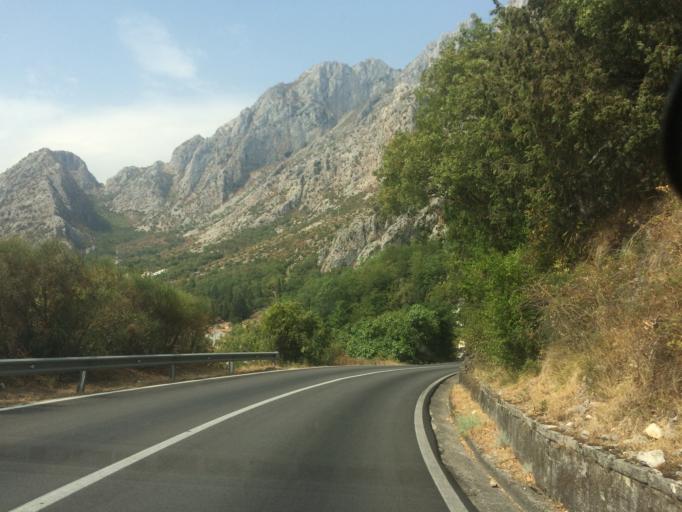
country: ME
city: Dobrota
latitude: 42.4872
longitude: 18.7654
